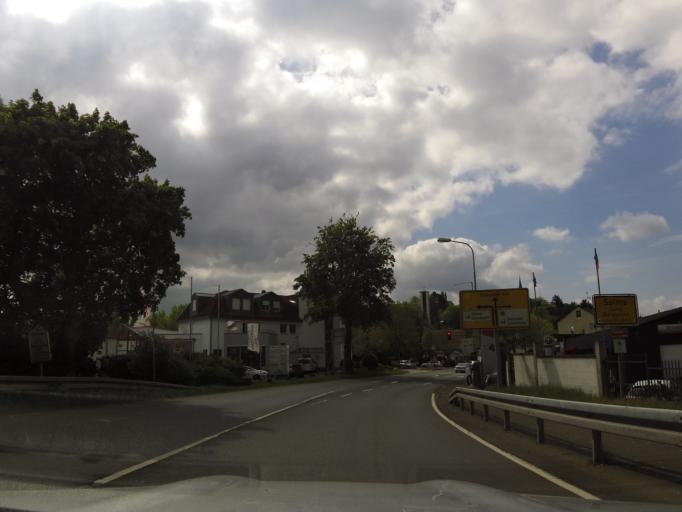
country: DE
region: Hesse
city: Burgsolms
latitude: 50.5437
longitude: 8.4089
